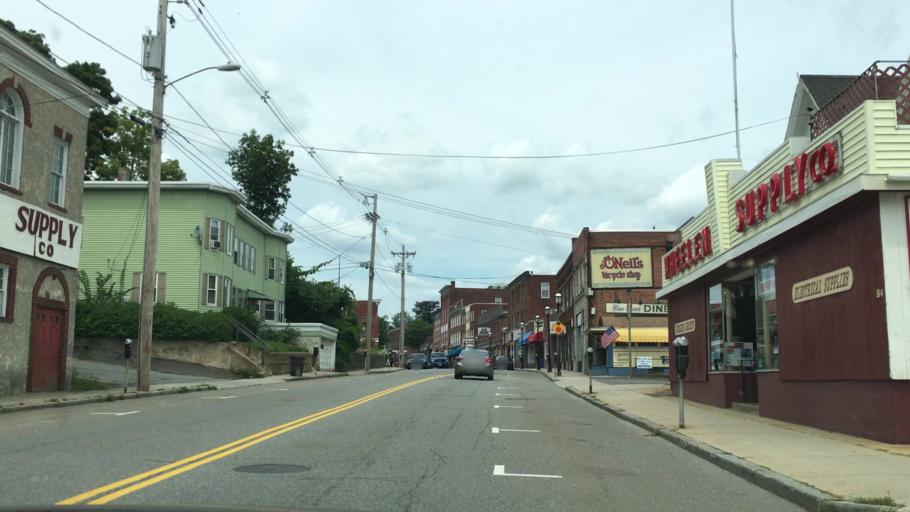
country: US
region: Massachusetts
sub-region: Worcester County
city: Gardner
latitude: 42.5737
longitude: -71.9945
